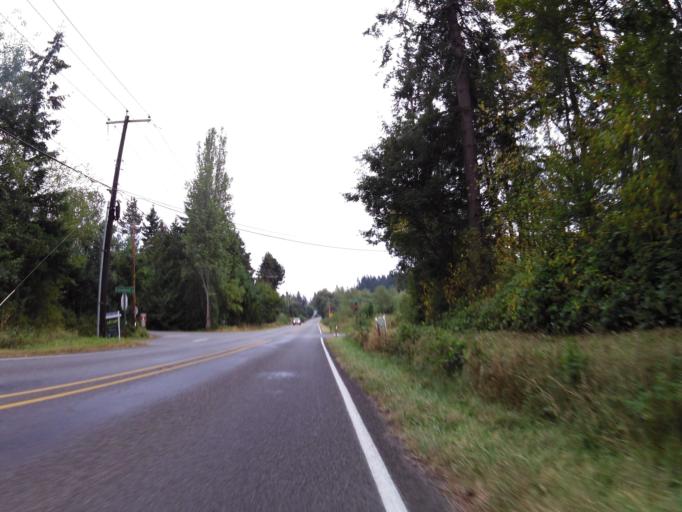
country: US
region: Washington
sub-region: Jefferson County
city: Port Hadlock-Irondale
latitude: 48.0207
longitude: -122.7353
